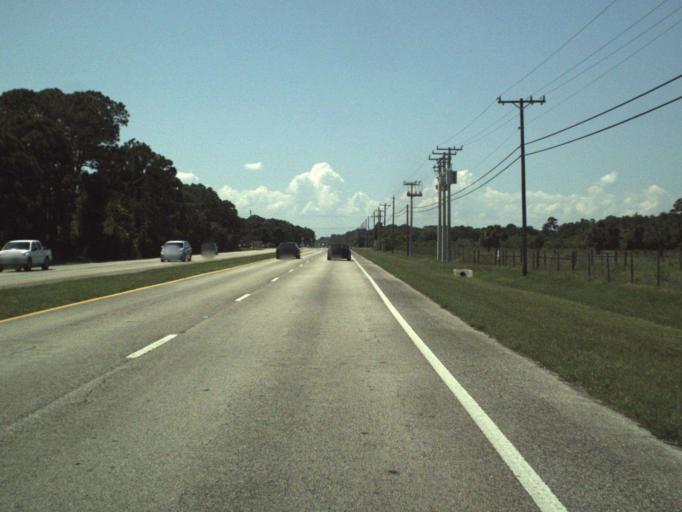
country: US
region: Florida
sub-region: Brevard County
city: Sharpes
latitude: 28.4516
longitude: -80.7093
